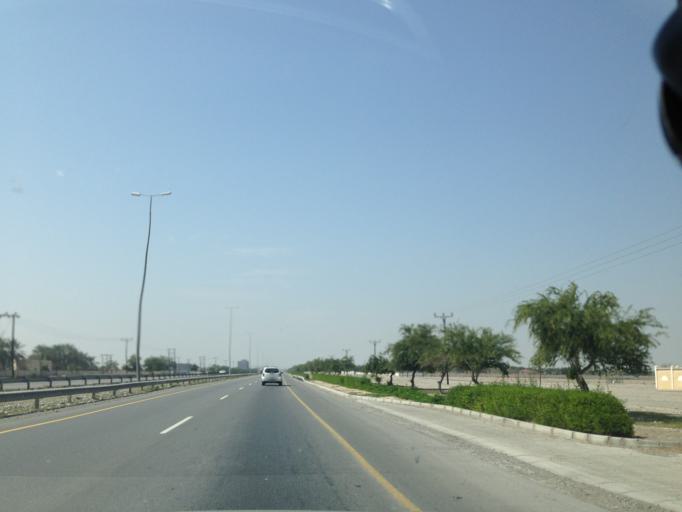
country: OM
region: Al Batinah
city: Barka'
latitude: 23.6597
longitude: 57.9214
